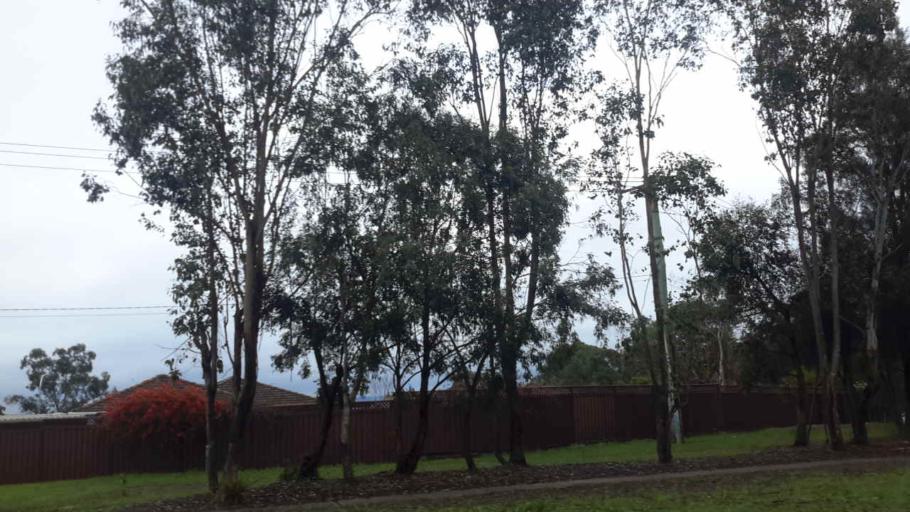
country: AU
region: New South Wales
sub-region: Penrith Municipality
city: Werrington Downs
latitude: -33.7355
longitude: 150.7174
